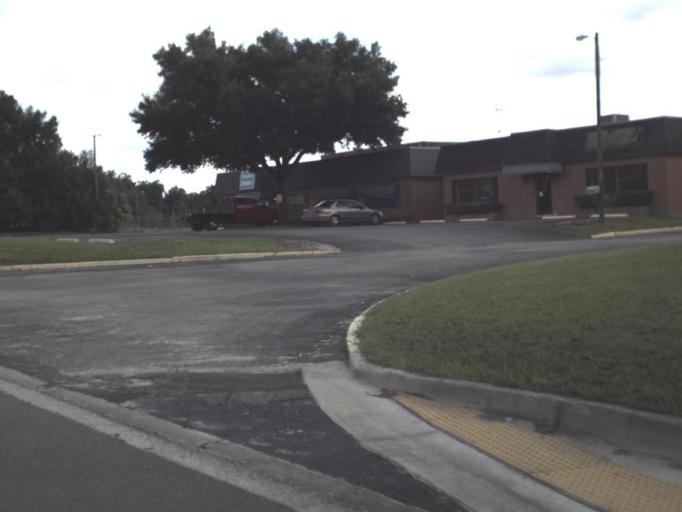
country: US
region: Florida
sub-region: Pasco County
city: Dade City
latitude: 28.3491
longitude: -82.1874
